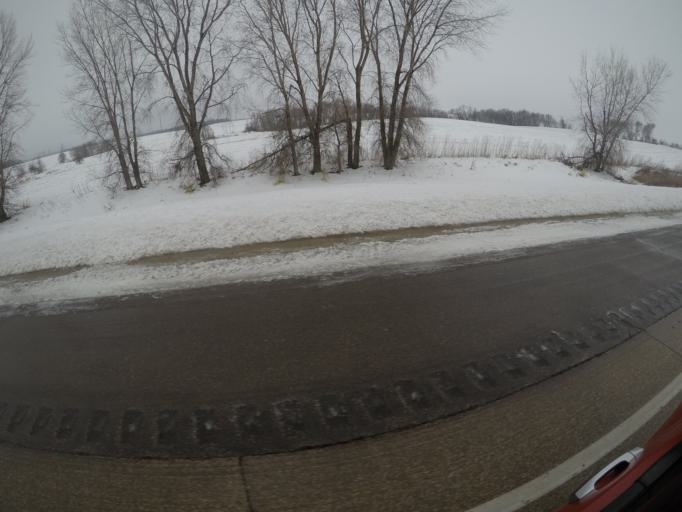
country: US
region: Minnesota
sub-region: Goodhue County
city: Pine Island
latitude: 44.2294
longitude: -92.6508
